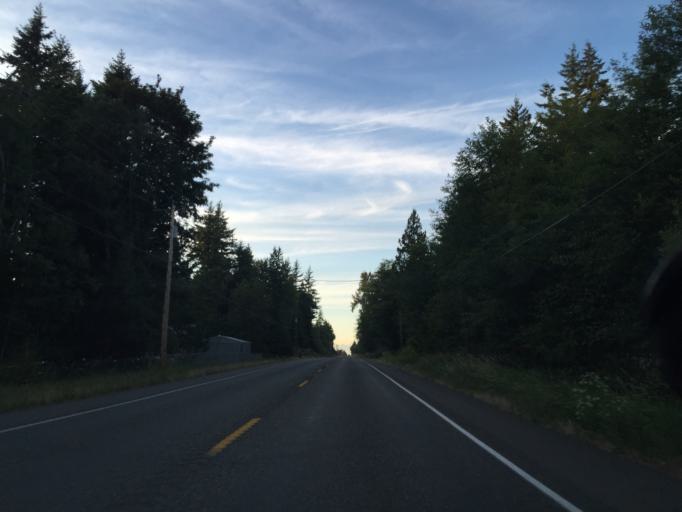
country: US
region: Washington
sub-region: Whatcom County
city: Everson
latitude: 48.8699
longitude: -122.3755
